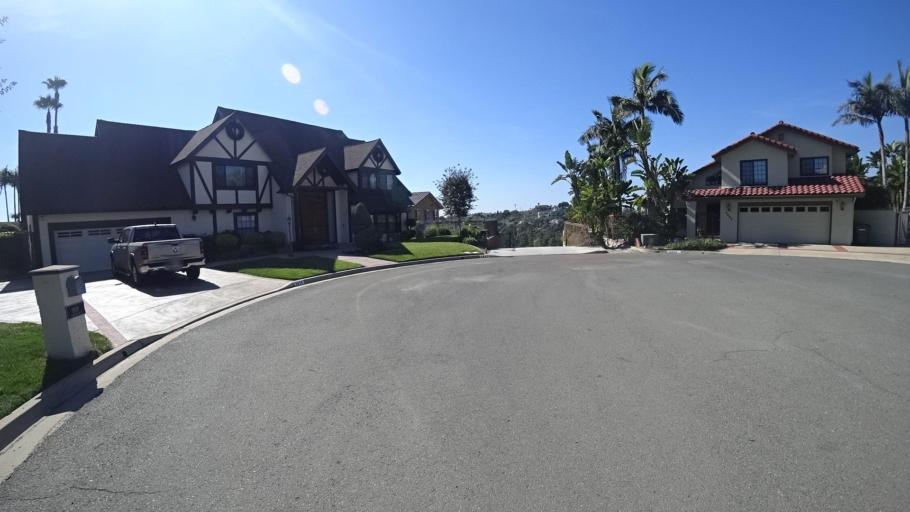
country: US
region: California
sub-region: San Diego County
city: Casa de Oro-Mount Helix
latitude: 32.7575
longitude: -116.9837
